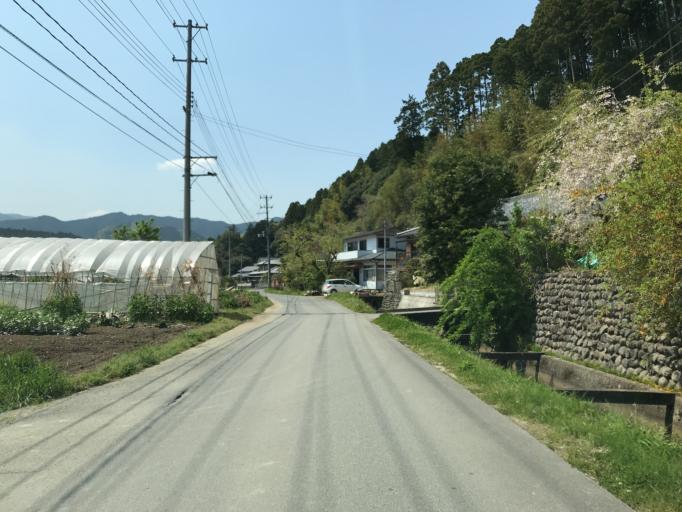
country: JP
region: Ibaraki
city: Kitaibaraki
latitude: 36.9281
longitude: 140.7467
